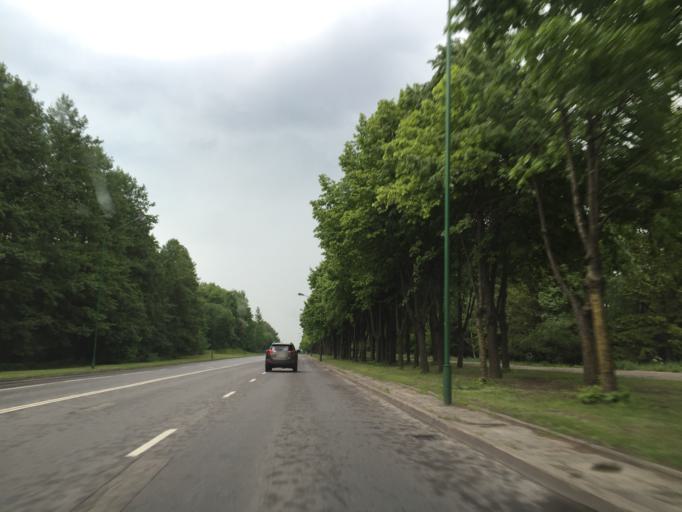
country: LT
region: Klaipedos apskritis
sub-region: Klaipeda
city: Klaipeda
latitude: 55.7373
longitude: 21.1298
